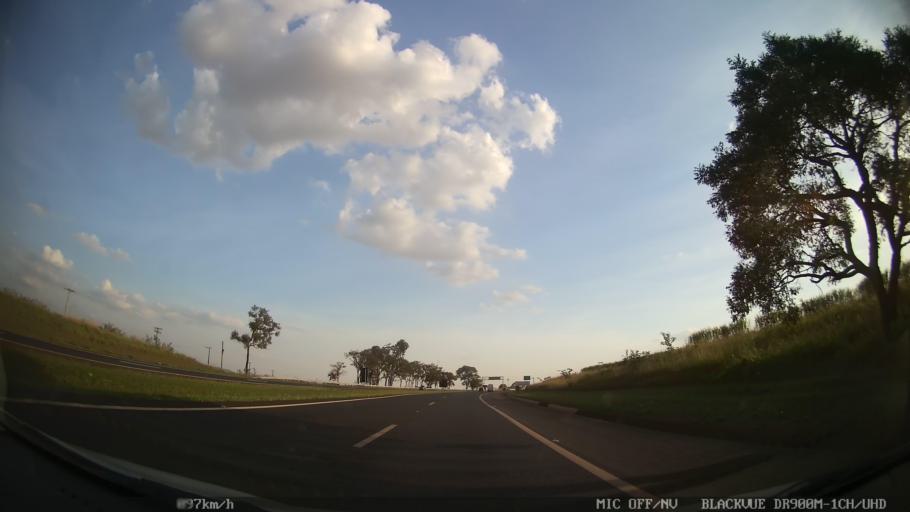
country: BR
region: Sao Paulo
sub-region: Ribeirao Preto
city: Ribeirao Preto
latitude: -21.1062
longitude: -47.7692
